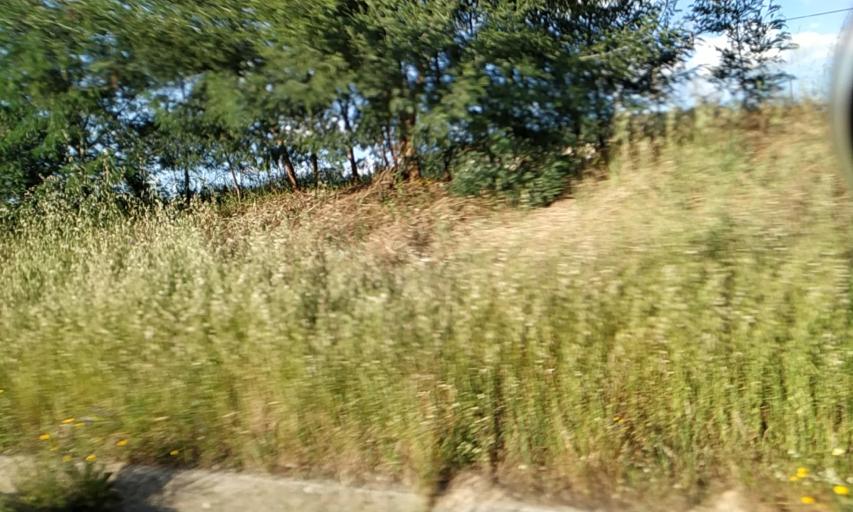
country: PT
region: Portalegre
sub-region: Portalegre
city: Portalegre
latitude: 39.3066
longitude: -7.4419
